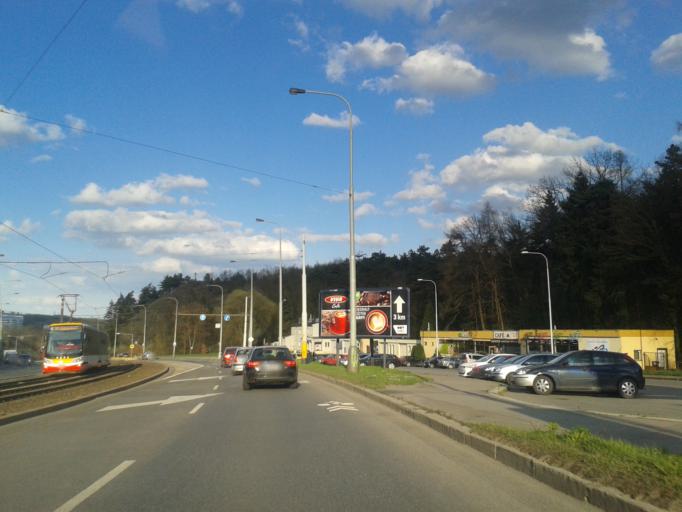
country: CZ
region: Central Bohemia
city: Hostivice
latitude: 50.0652
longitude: 14.3236
